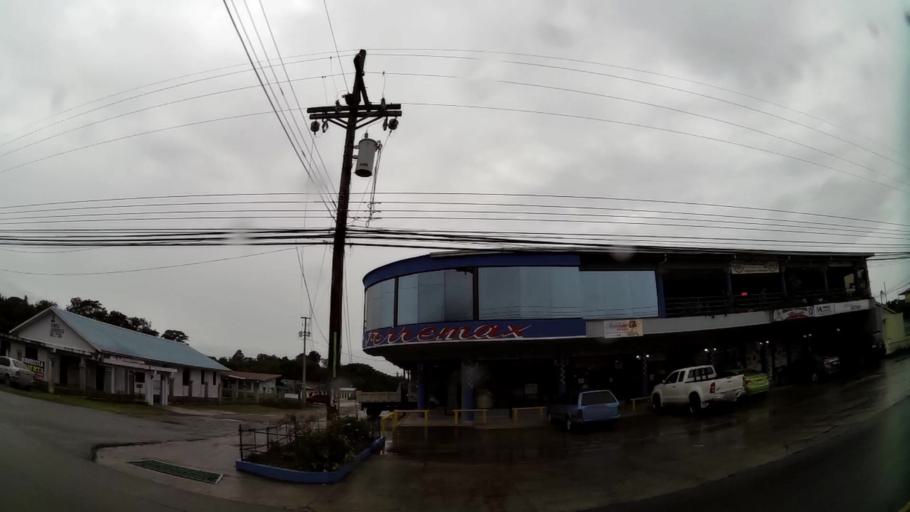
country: PA
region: Chiriqui
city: Volcan
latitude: 8.7778
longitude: -82.6432
